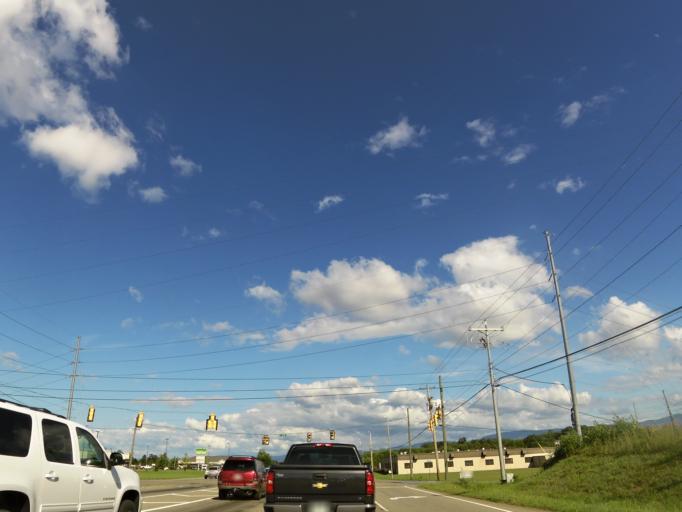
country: US
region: Tennessee
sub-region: Greene County
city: Greeneville
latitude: 36.1791
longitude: -82.8102
